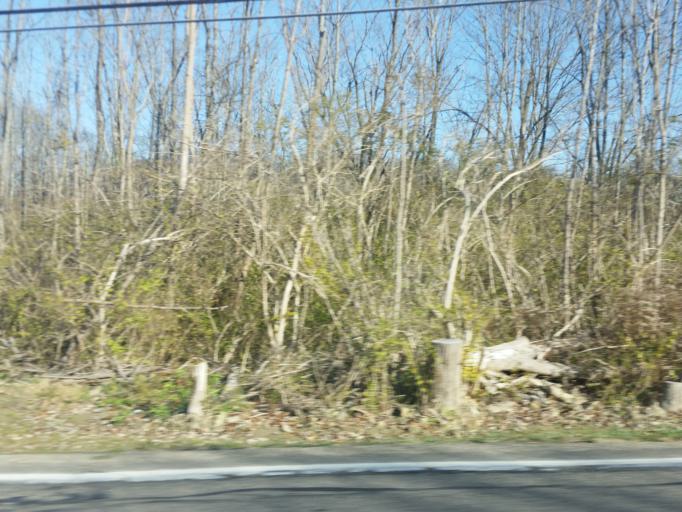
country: US
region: Ohio
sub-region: Butler County
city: Oxford
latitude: 39.4848
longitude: -84.7172
